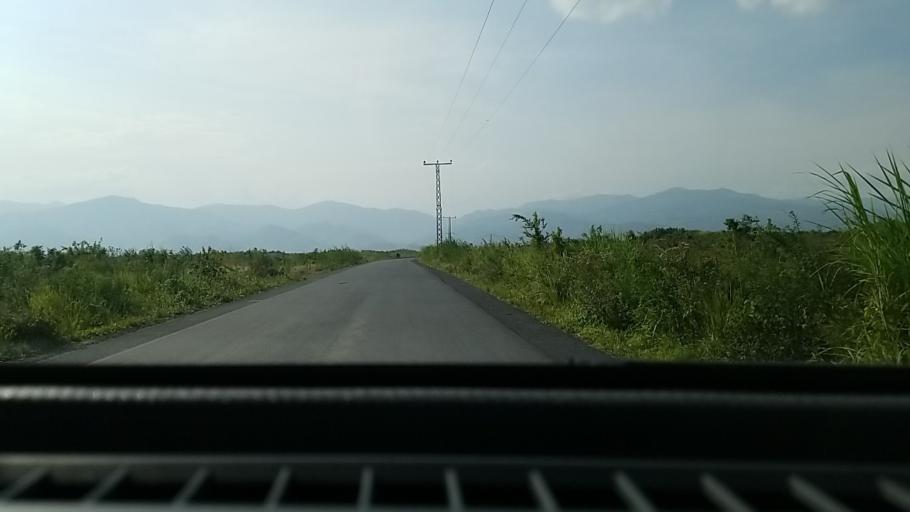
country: CD
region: Nord Kivu
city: Sake
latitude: -1.5945
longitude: 29.1018
